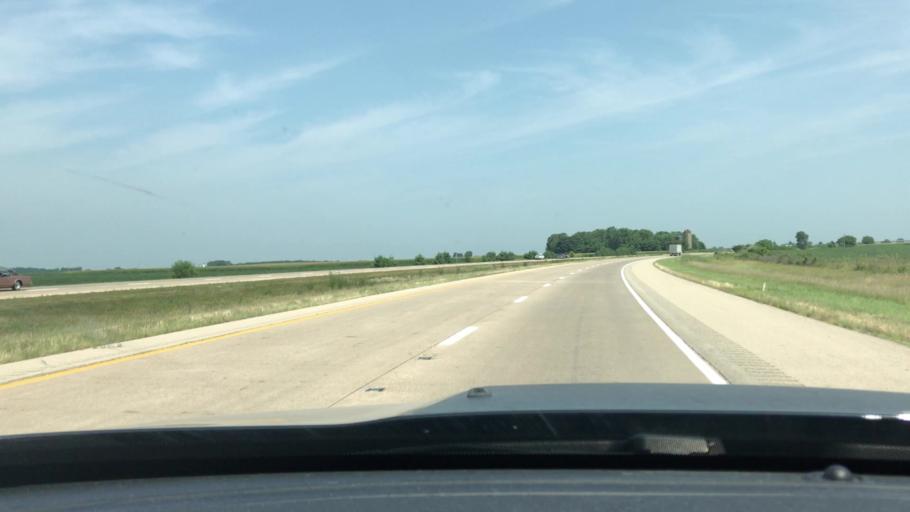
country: US
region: Illinois
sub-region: LaSalle County
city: La Salle
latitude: 41.4415
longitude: -89.0587
